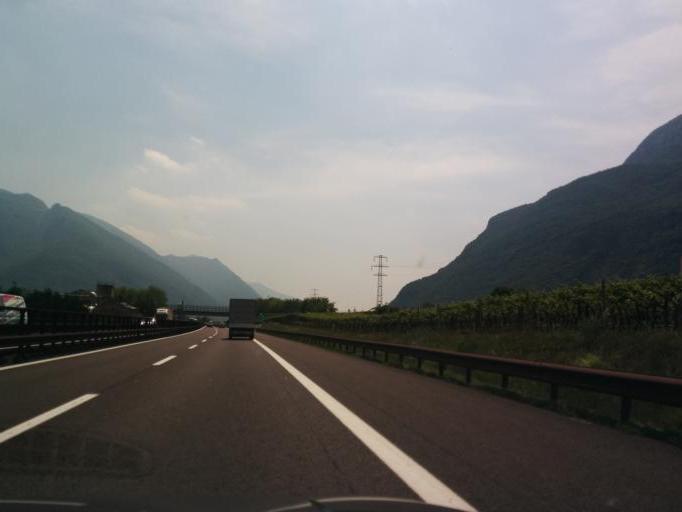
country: IT
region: Veneto
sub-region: Provincia di Verona
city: Rivalta
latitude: 45.6635
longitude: 10.8946
